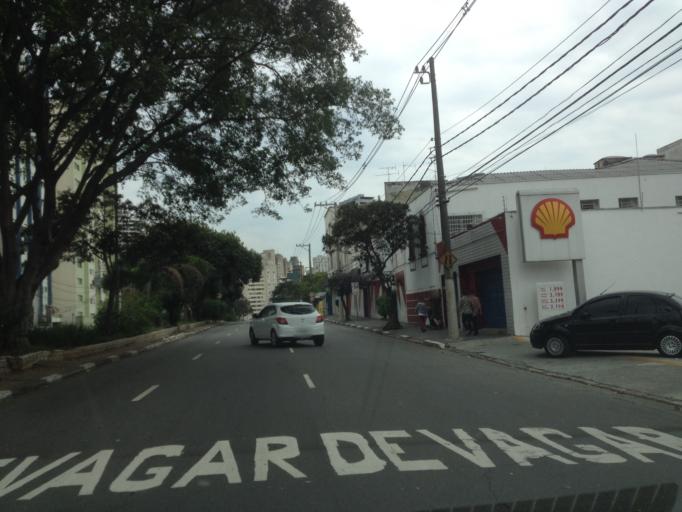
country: BR
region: Sao Paulo
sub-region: Sao Paulo
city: Sao Paulo
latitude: -23.5553
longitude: -46.6457
